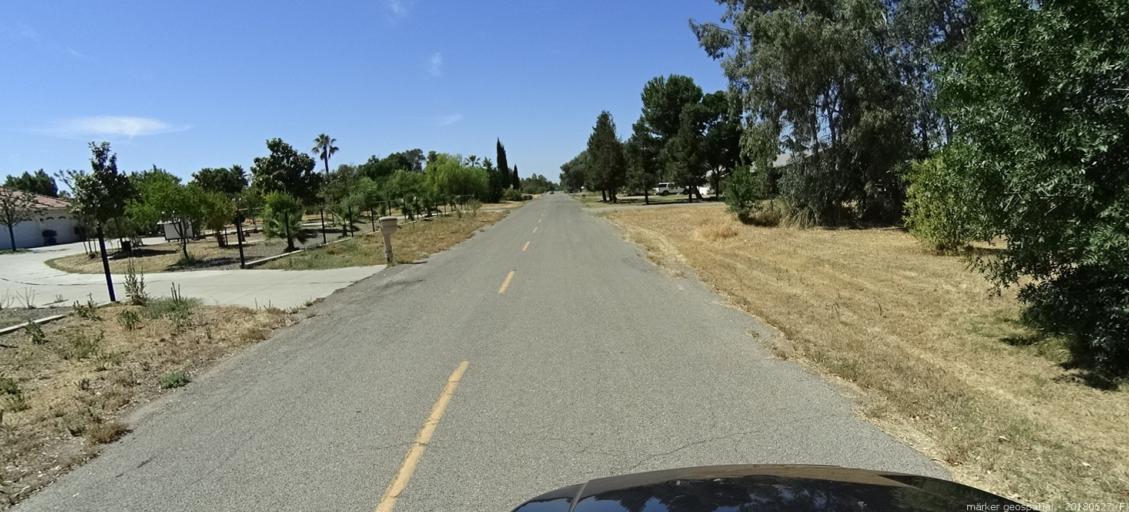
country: US
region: California
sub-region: Madera County
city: Bonadelle Ranchos-Madera Ranchos
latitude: 36.9362
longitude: -119.8795
